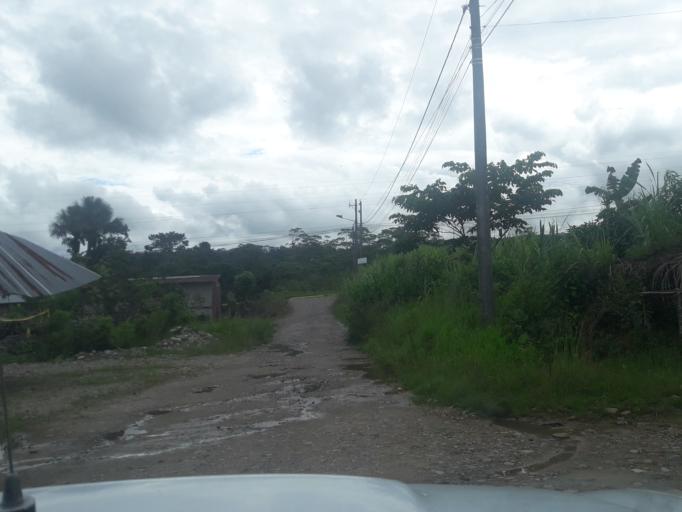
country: EC
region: Napo
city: Archidona
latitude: -0.9512
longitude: -77.8159
